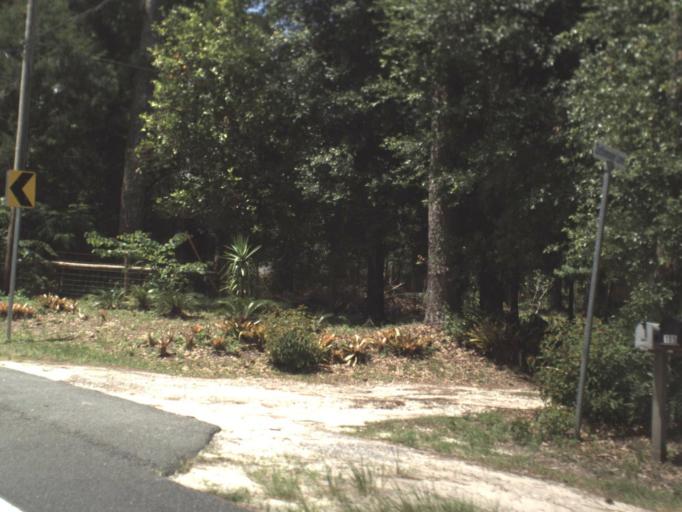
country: US
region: Florida
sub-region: Clay County
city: Keystone Heights
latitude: 29.6905
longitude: -82.0396
